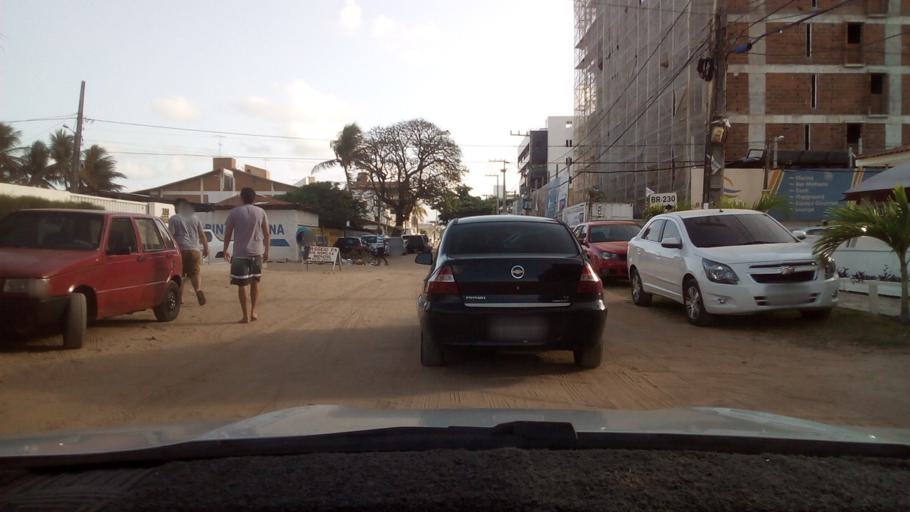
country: BR
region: Paraiba
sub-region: Cabedelo
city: Cabedelo
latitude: -7.0085
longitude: -34.8274
